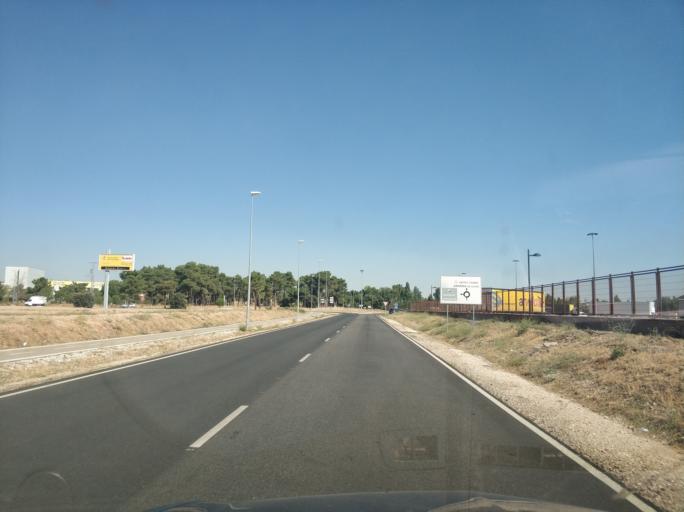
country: ES
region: Castille and Leon
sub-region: Provincia de Burgos
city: Aranda de Duero
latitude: 41.6706
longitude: -3.7000
